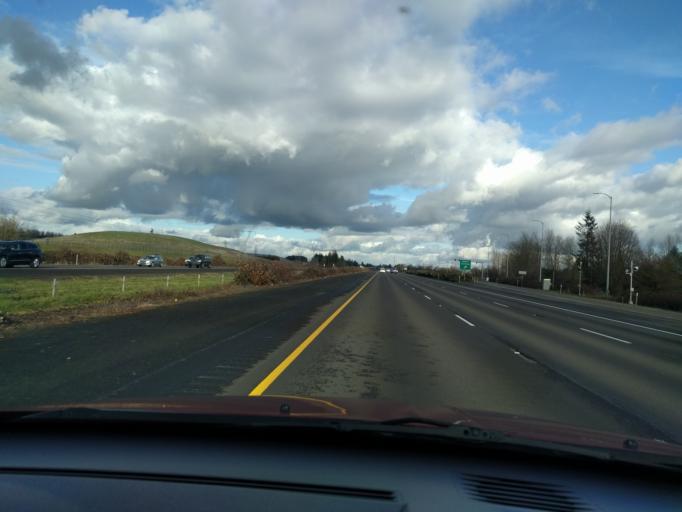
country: US
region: Oregon
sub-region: Marion County
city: Woodburn
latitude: 45.1729
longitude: -122.8583
